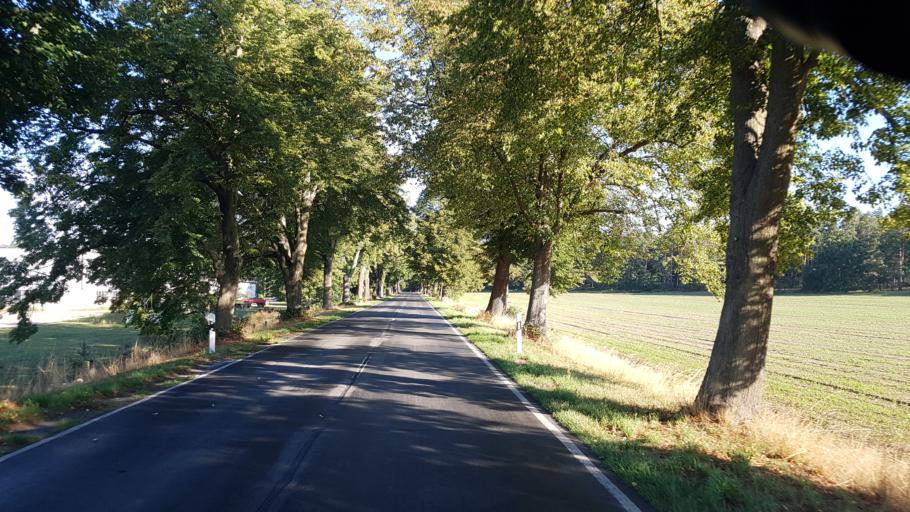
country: DE
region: Brandenburg
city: Bronkow
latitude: 51.6577
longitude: 13.9201
